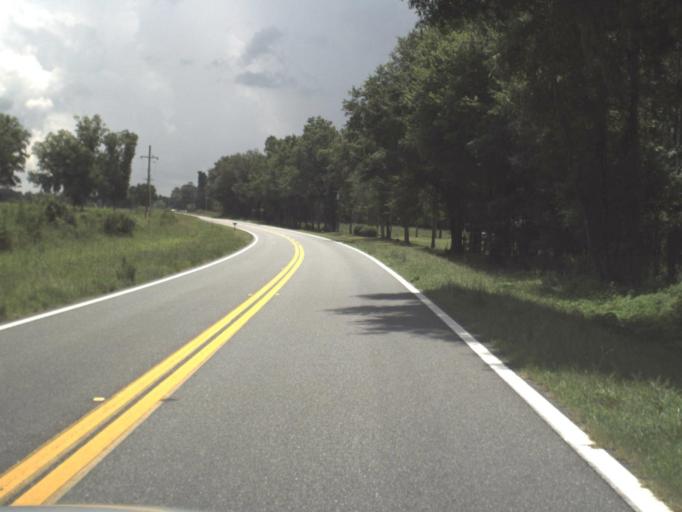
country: US
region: Florida
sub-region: Union County
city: Lake Butler
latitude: 29.8914
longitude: -82.3481
